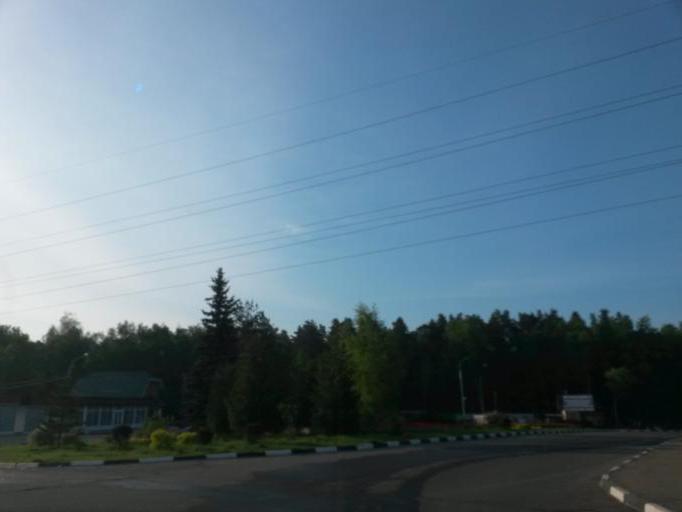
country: RU
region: Moskovskaya
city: Shcherbinka
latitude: 55.5055
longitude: 37.6173
